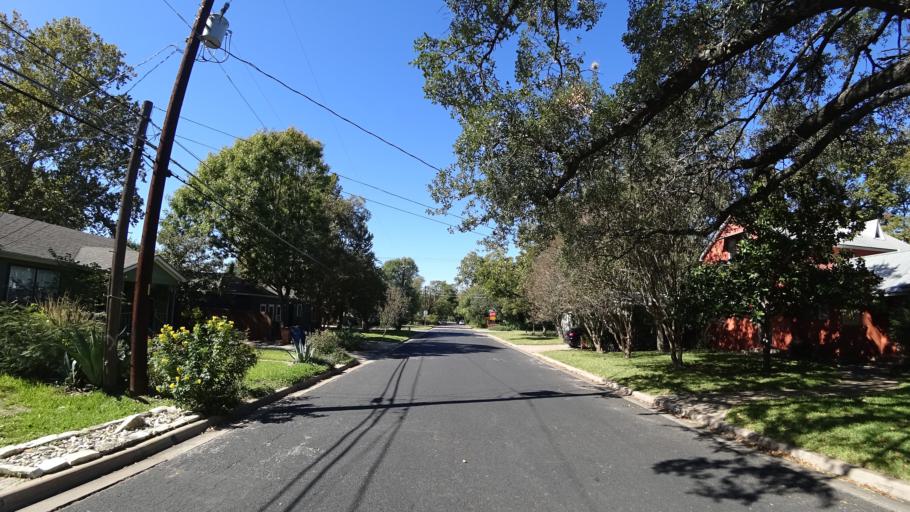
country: US
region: Texas
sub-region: Travis County
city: Austin
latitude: 30.3280
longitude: -97.7435
